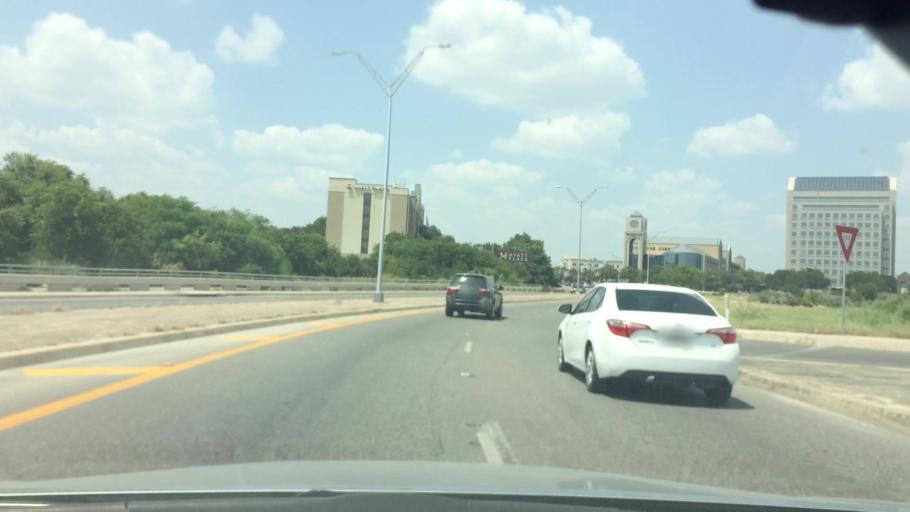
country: US
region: Texas
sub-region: Bexar County
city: Alamo Heights
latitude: 29.5014
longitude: -98.4821
